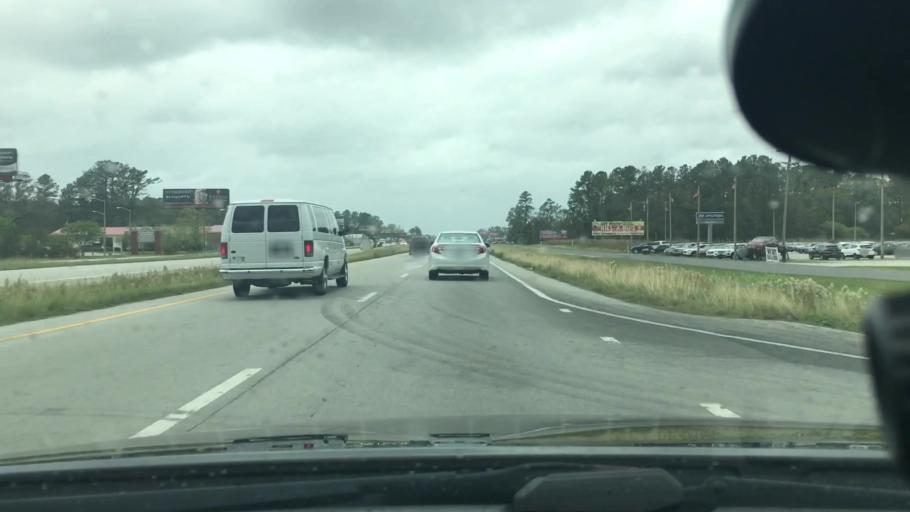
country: US
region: North Carolina
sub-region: Craven County
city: James City
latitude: 35.0564
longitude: -77.0175
